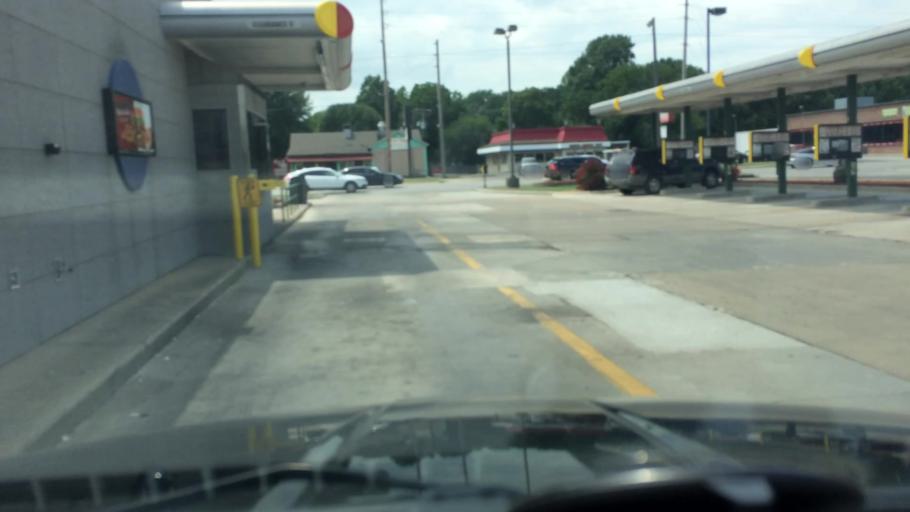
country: US
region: Missouri
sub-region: Greene County
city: Springfield
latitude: 37.2277
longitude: -93.2607
